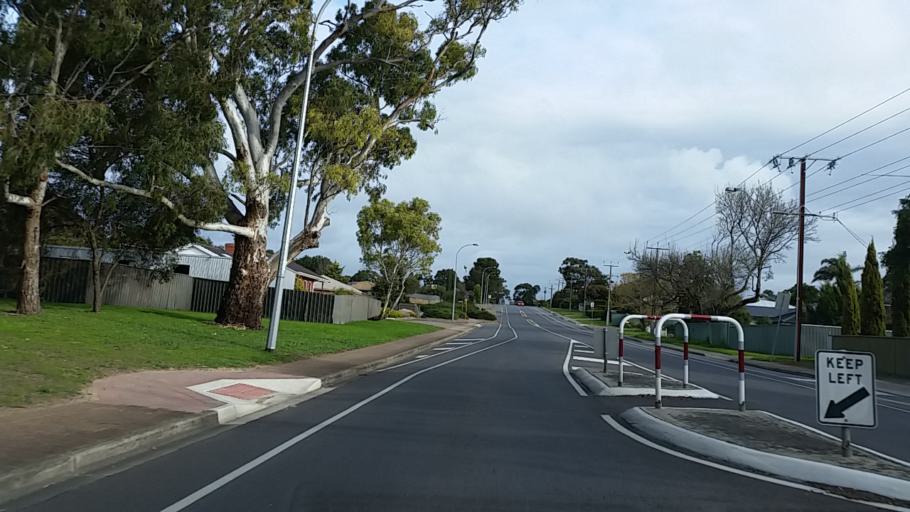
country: AU
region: South Australia
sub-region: Onkaparinga
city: Morphett Vale
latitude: -35.1390
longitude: 138.5374
